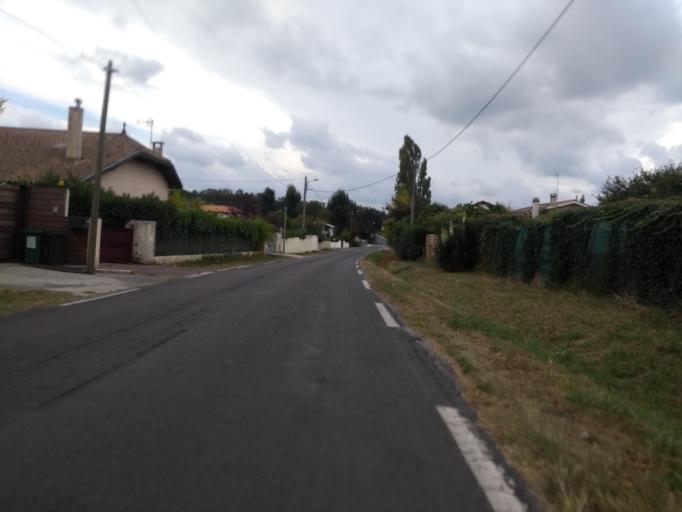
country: FR
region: Aquitaine
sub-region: Departement de la Gironde
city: Pessac
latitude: 44.8136
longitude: -0.6561
